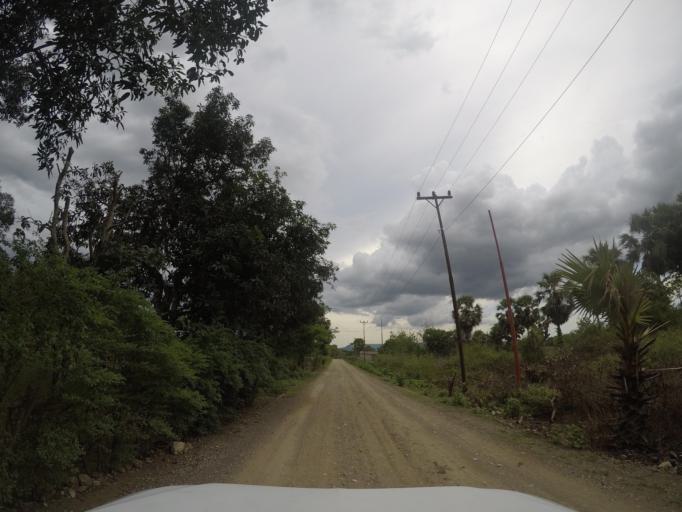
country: TL
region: Bobonaro
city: Maliana
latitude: -8.9941
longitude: 125.2052
